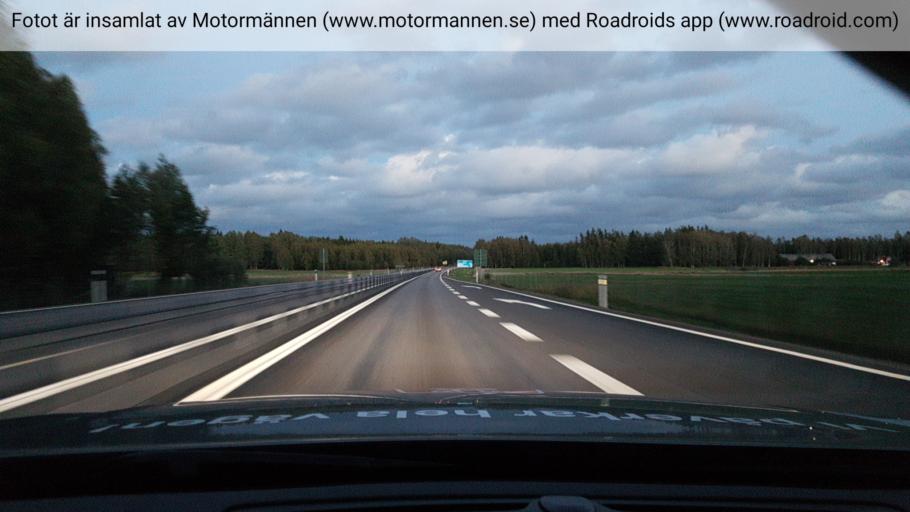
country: SE
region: Vaermland
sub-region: Karlstads Kommun
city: Skattkarr
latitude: 59.3889
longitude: 13.8599
